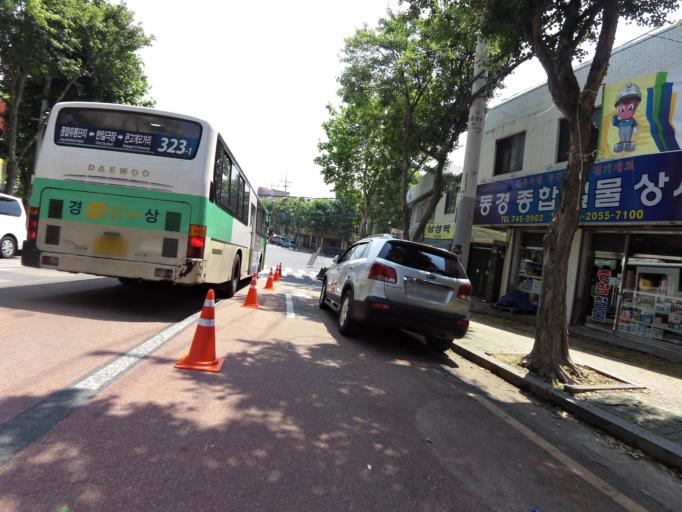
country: KR
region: Daegu
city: Daegu
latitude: 35.8642
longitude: 128.6432
